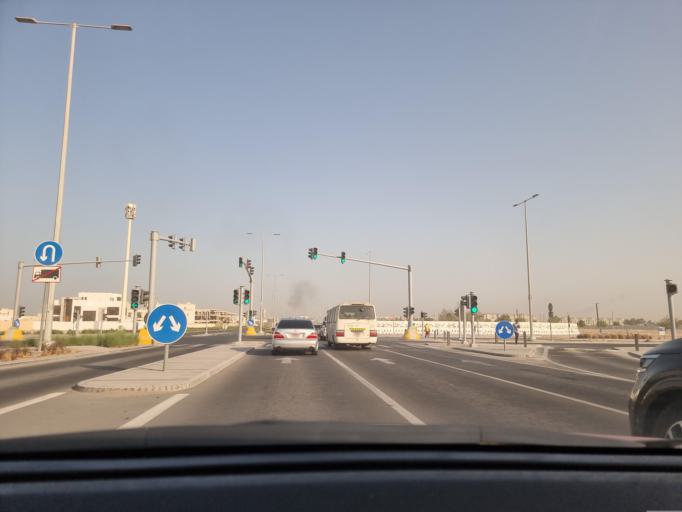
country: AE
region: Abu Dhabi
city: Abu Dhabi
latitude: 24.4234
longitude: 54.6074
